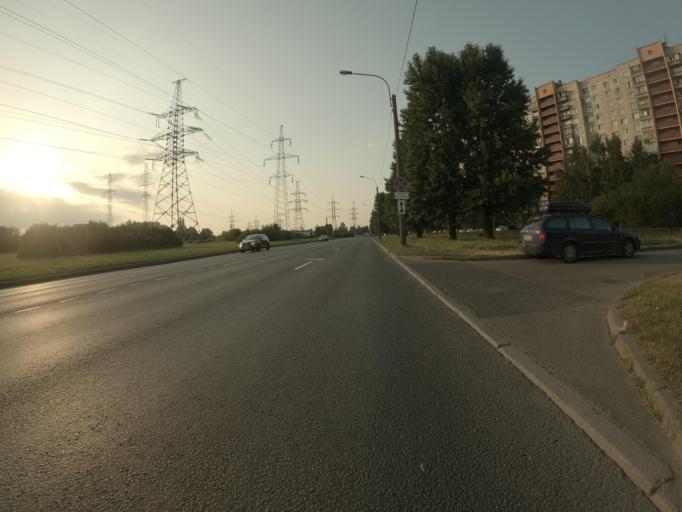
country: RU
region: St.-Petersburg
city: Krasnogvargeisky
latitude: 59.9510
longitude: 30.4608
